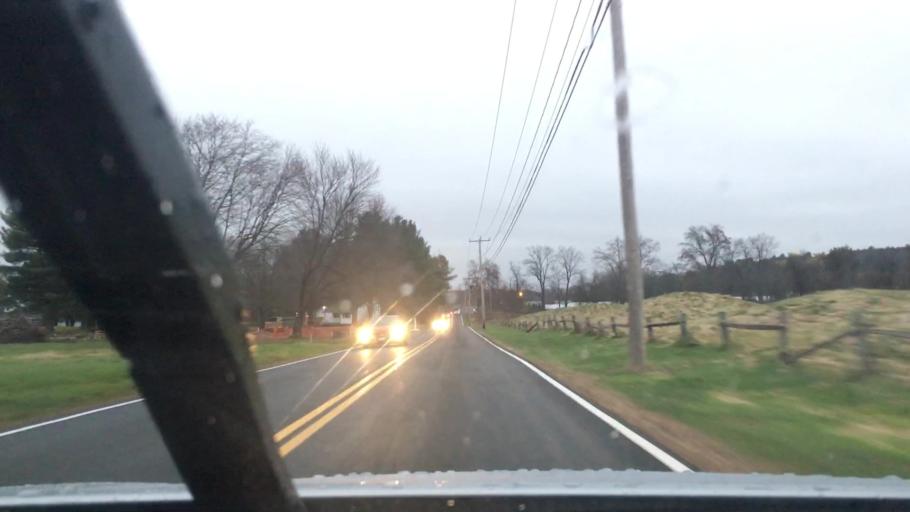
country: US
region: Massachusetts
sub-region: Hampden County
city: Southwick
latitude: 42.0813
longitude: -72.7709
